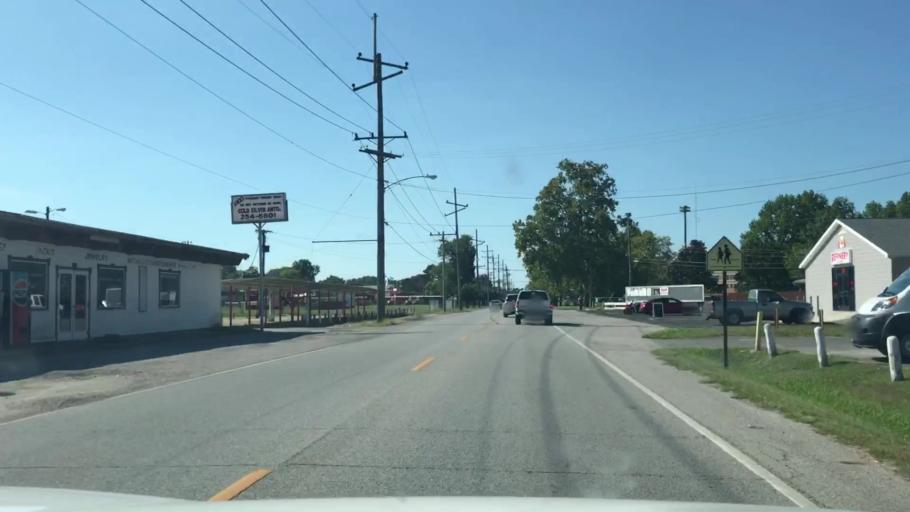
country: US
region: Illinois
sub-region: Madison County
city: Wood River
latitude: 38.8709
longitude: -90.0930
